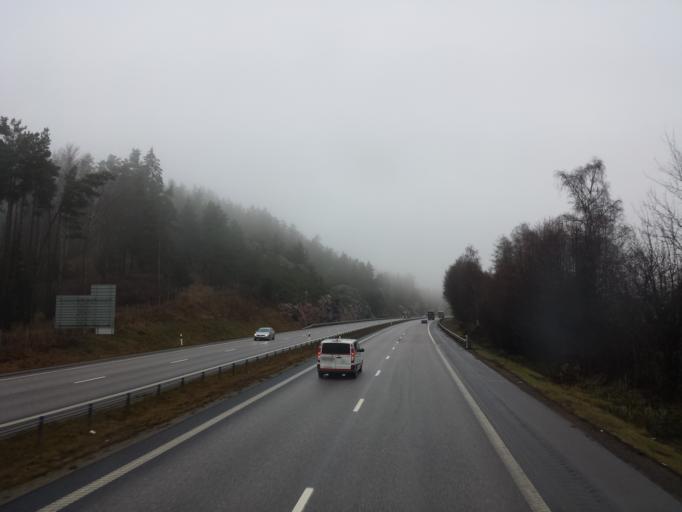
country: SE
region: OEstergoetland
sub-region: Norrkopings Kommun
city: Krokek
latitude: 58.6947
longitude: 16.3366
